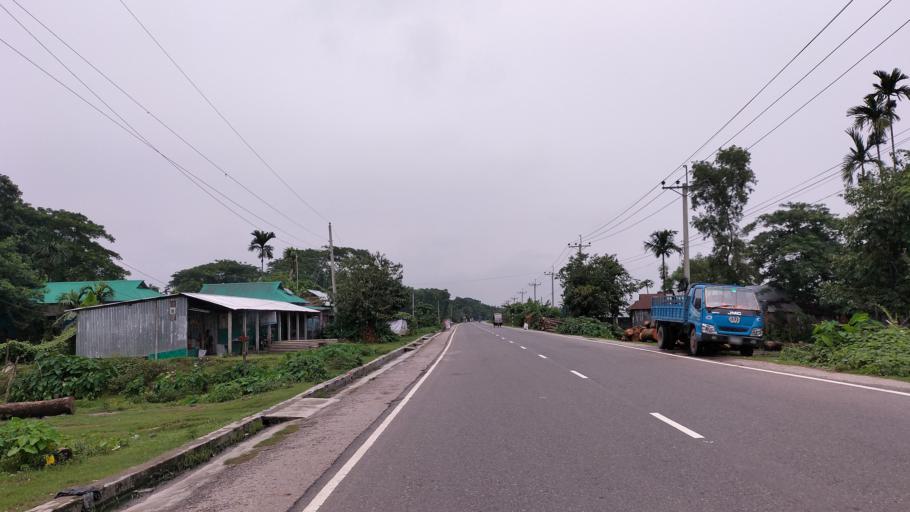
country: BD
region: Dhaka
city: Netrakona
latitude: 24.8525
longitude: 90.6149
